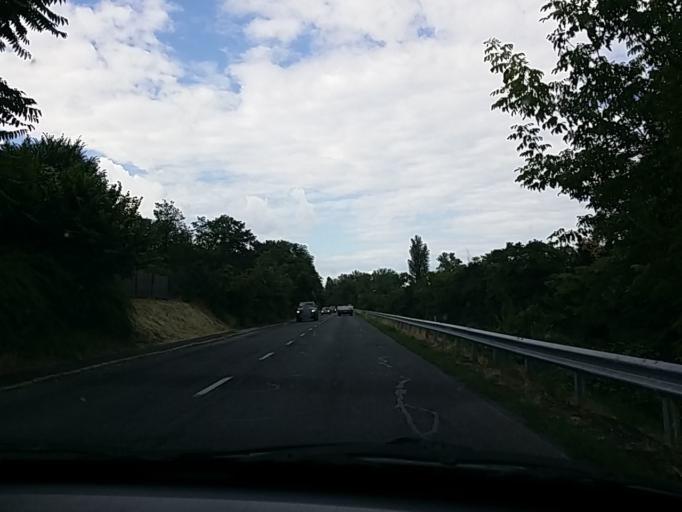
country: HU
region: Veszprem
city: Zanka
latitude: 46.8544
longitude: 17.6669
